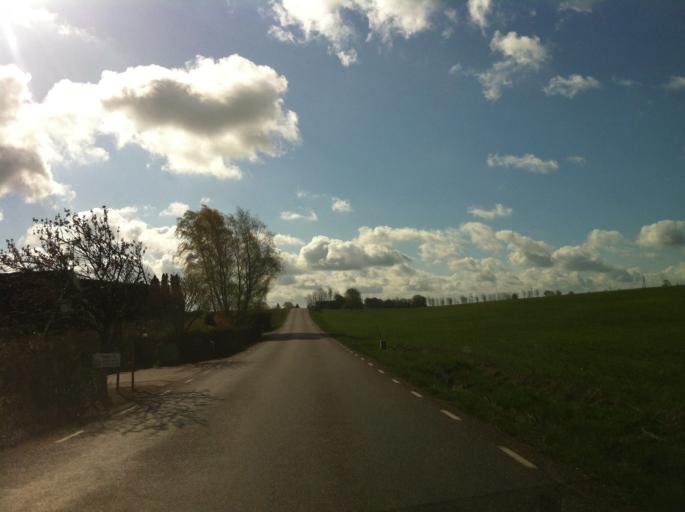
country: SE
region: Skane
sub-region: Eslovs Kommun
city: Stehag
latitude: 55.9230
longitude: 13.3767
